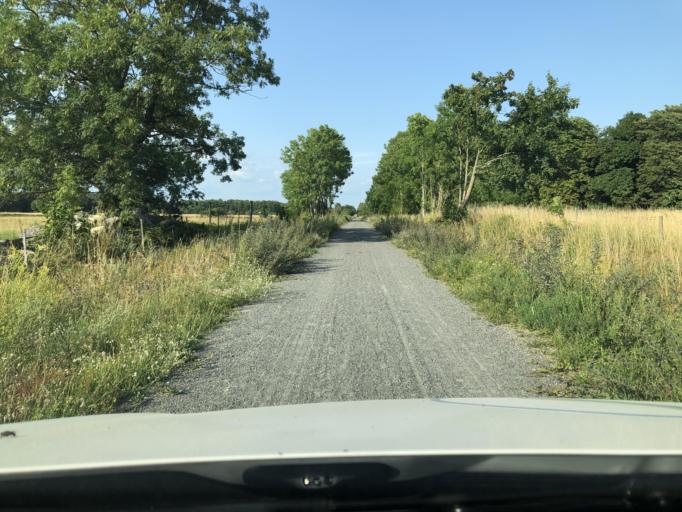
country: SE
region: Skane
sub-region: Kristianstads Kommun
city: Norra Asum
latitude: 55.9386
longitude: 14.1412
